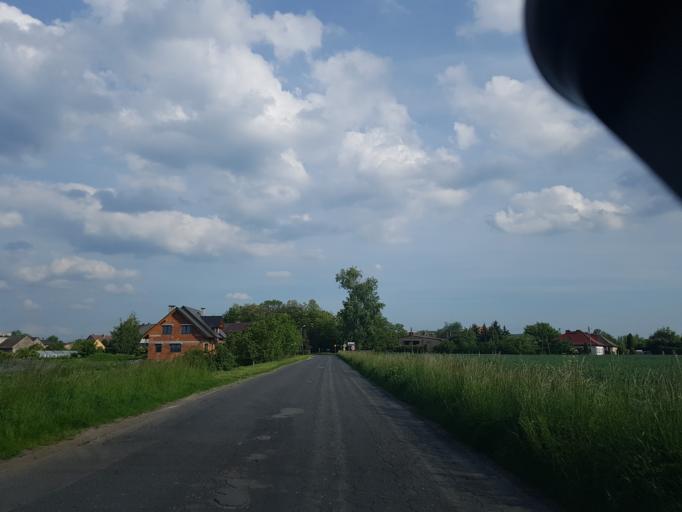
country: PL
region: Lower Silesian Voivodeship
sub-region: Powiat strzelinski
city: Wiazow
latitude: 50.8566
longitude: 17.1821
